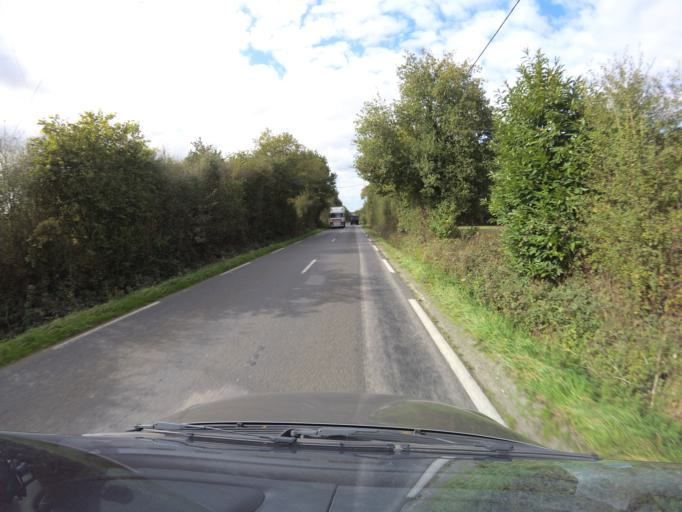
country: FR
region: Pays de la Loire
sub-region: Departement de la Loire-Atlantique
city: Fay-de-Bretagne
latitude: 47.4096
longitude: -1.7607
